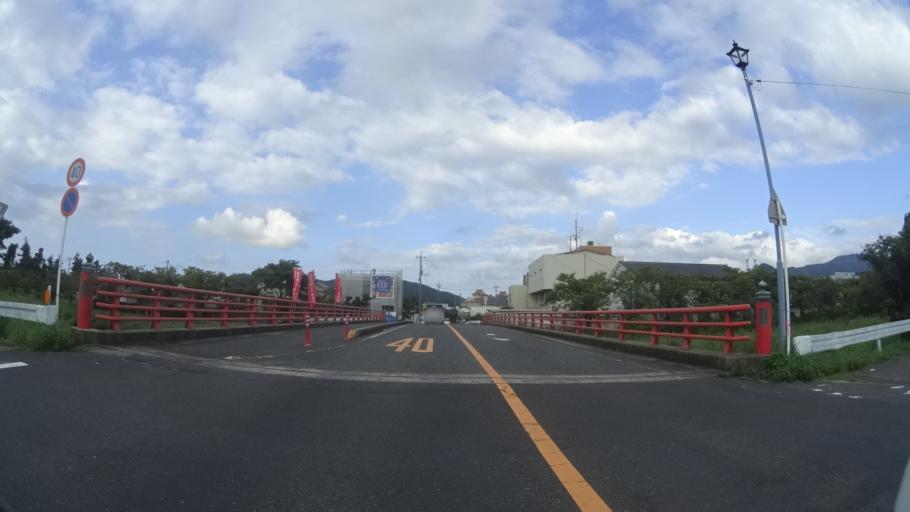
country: JP
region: Tottori
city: Kurayoshi
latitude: 35.4674
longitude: 133.8952
